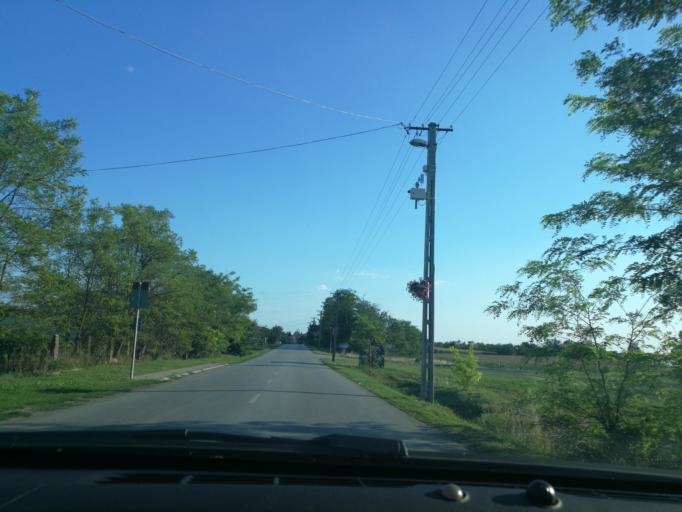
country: HU
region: Szabolcs-Szatmar-Bereg
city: Buj
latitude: 48.1160
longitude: 21.6560
